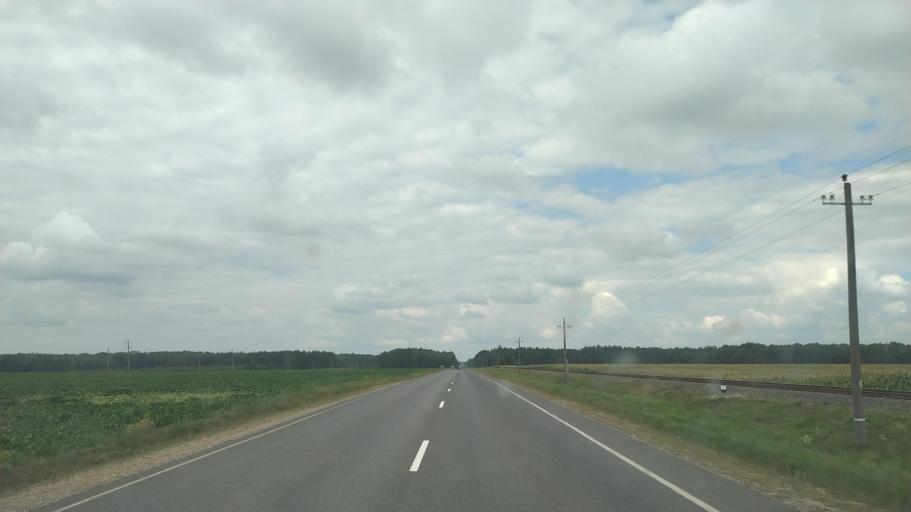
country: BY
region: Brest
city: Byelaazyorsk
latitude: 52.5157
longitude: 25.1536
